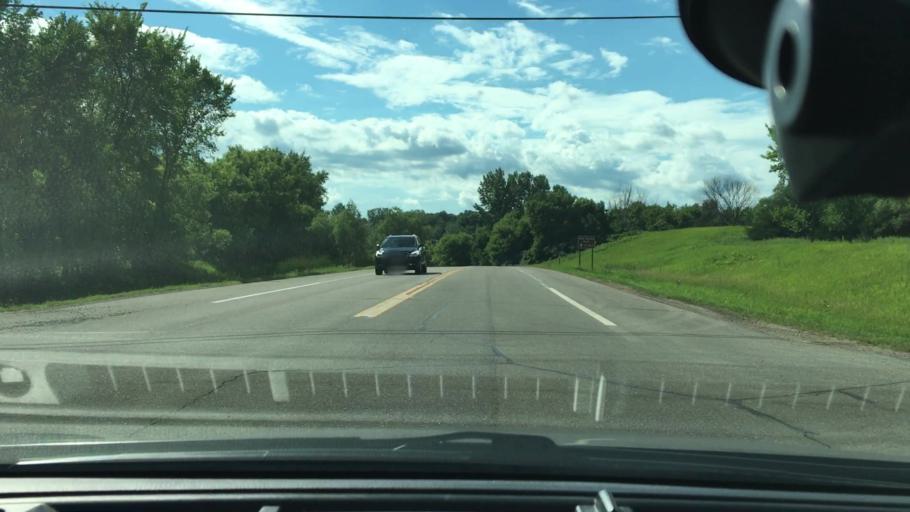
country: US
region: Minnesota
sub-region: Hennepin County
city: Minnetrista
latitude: 44.9236
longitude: -93.7014
